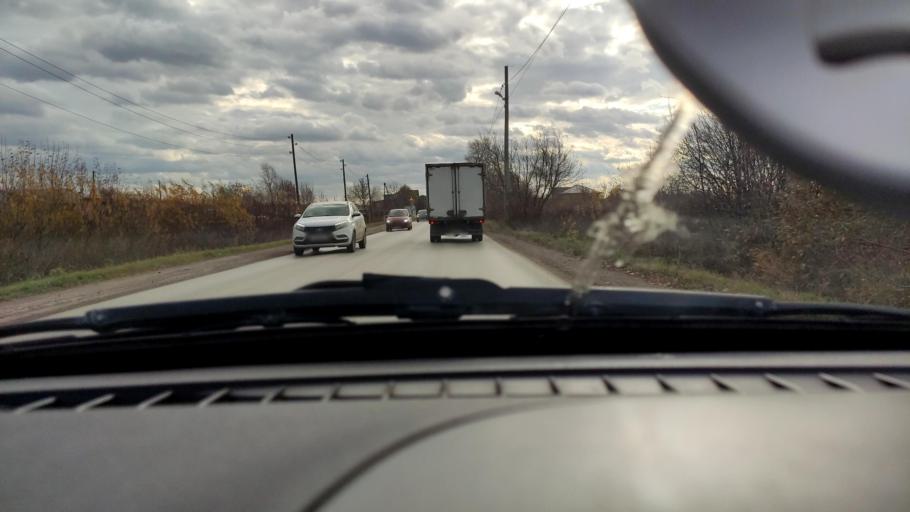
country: RU
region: Perm
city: Kondratovo
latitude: 57.9686
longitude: 56.1164
